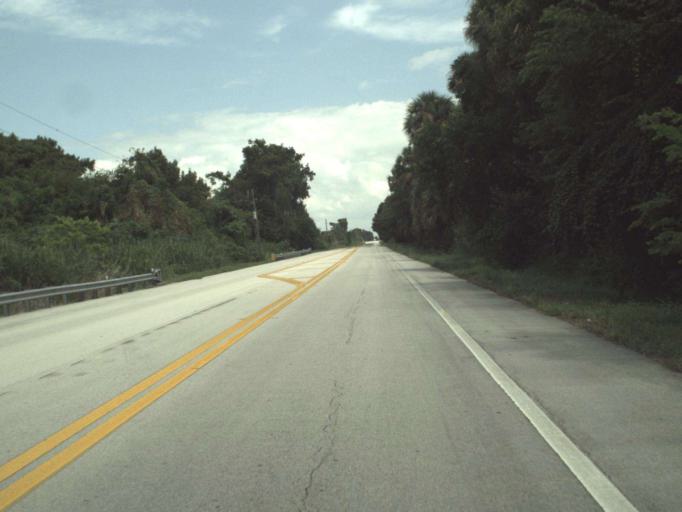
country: US
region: Florida
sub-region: Martin County
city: Indiantown
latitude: 27.0532
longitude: -80.6442
